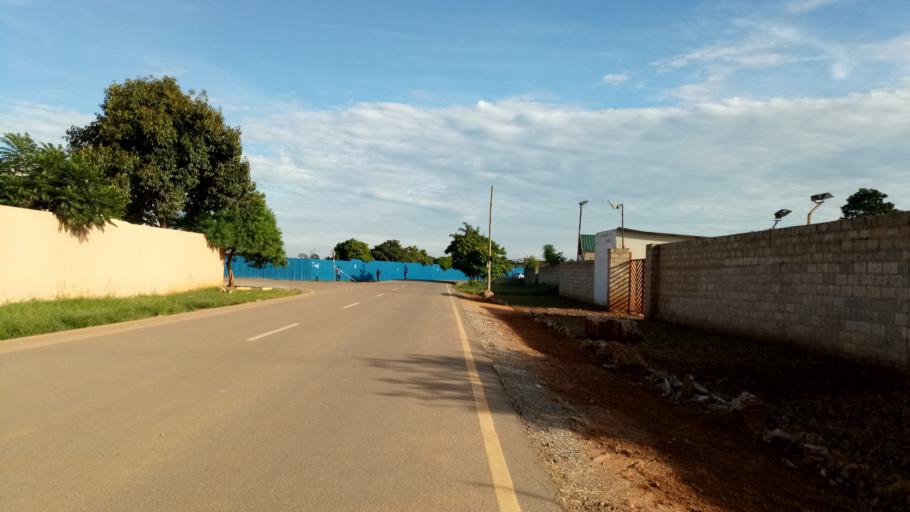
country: ZM
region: Lusaka
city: Lusaka
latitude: -15.4465
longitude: 28.3190
